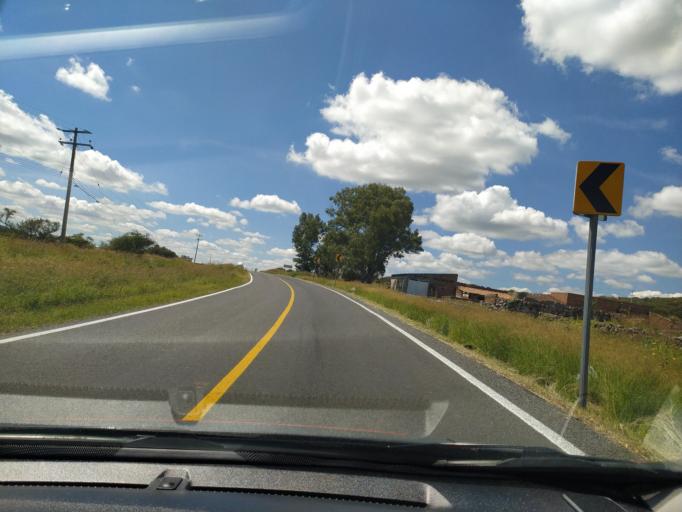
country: MX
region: Jalisco
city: San Miguel el Alto
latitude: 21.0251
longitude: -102.4293
